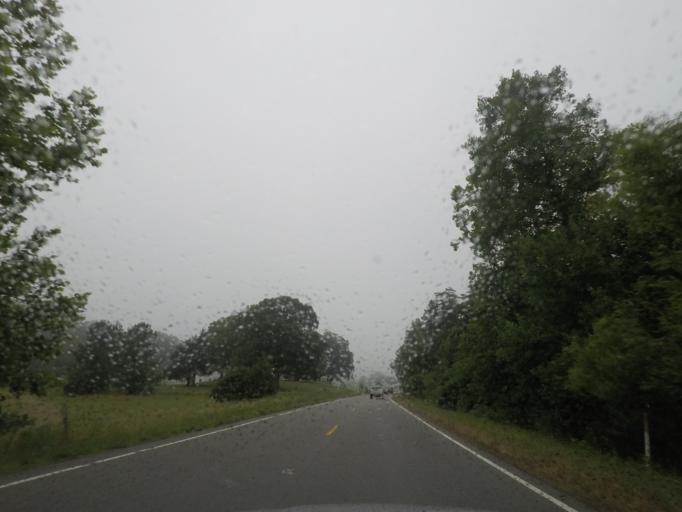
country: US
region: Virginia
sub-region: Prince Edward County
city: Farmville
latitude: 37.3859
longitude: -78.4851
